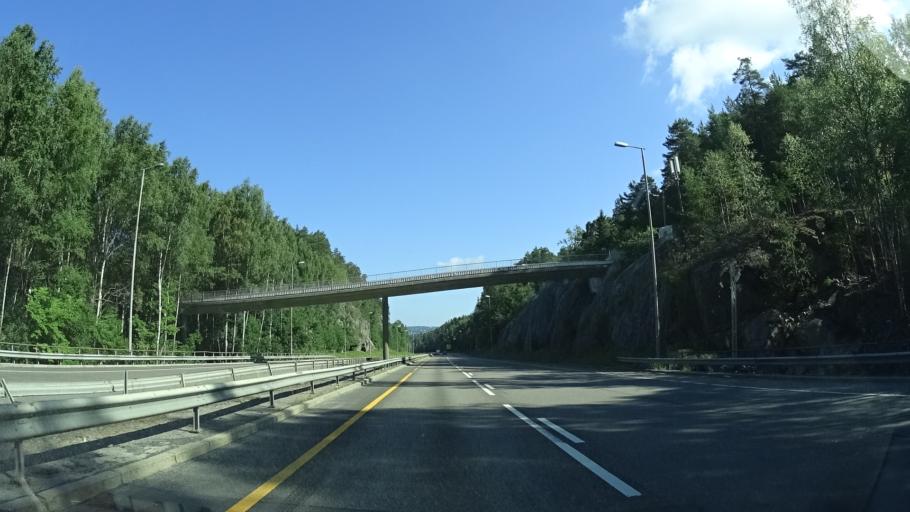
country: NO
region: Akershus
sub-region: Oppegard
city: Kolbotn
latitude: 59.8271
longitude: 10.7774
